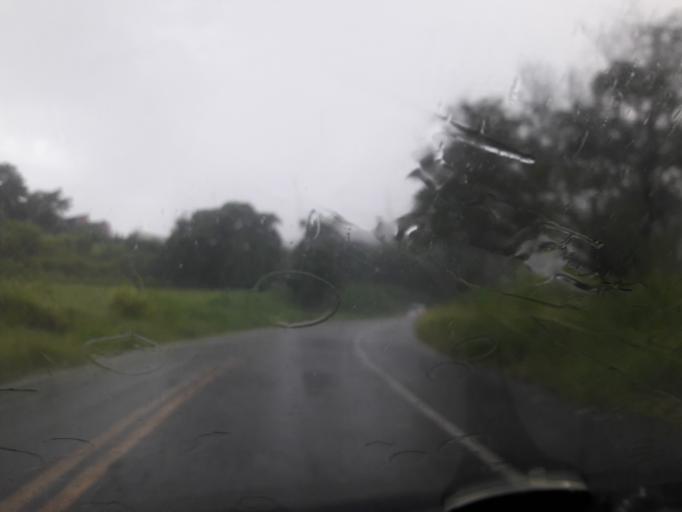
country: BR
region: Sao Paulo
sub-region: Bom Jesus Dos Perdoes
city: Bom Jesus dos Perdoes
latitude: -23.1774
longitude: -46.3966
